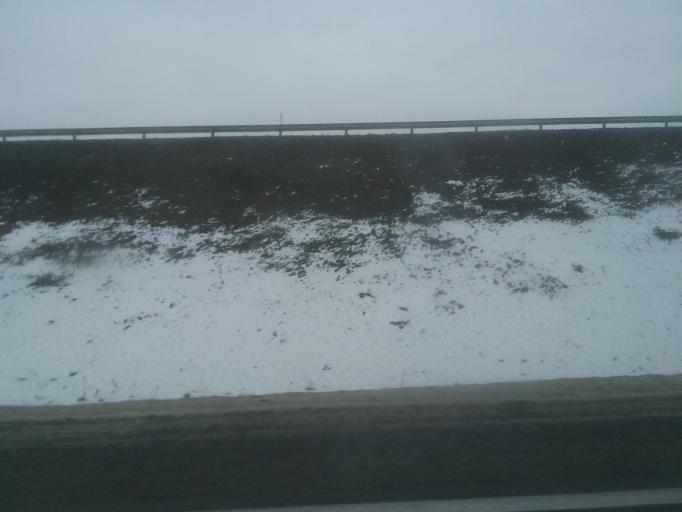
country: RU
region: Tula
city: Brusyanka
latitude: 54.0134
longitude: 38.0098
